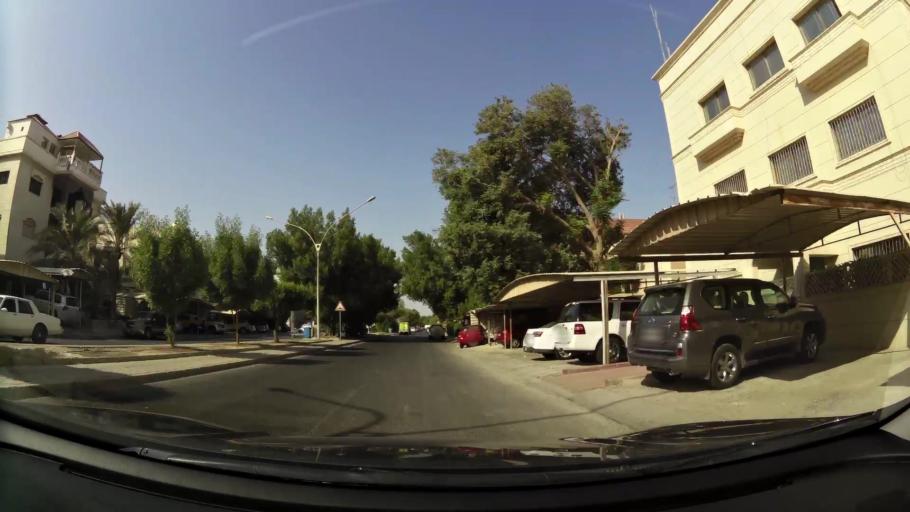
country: KW
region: Muhafazat Hawalli
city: Salwa
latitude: 29.2928
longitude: 48.0834
